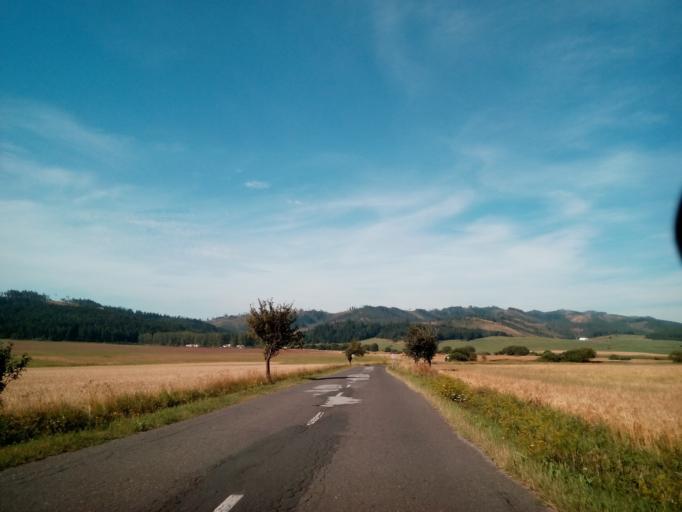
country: SK
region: Presovsky
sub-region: Okres Poprad
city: Poprad
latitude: 49.0382
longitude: 20.2725
